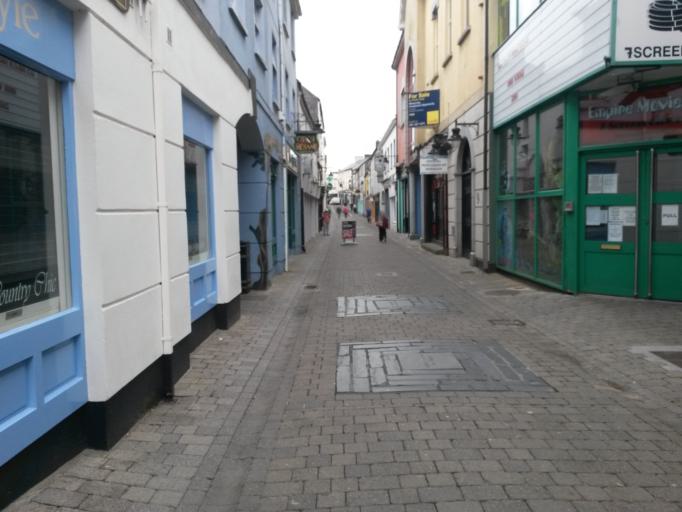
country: IE
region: Munster
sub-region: An Clar
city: Ennis
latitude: 52.8439
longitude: -8.9854
